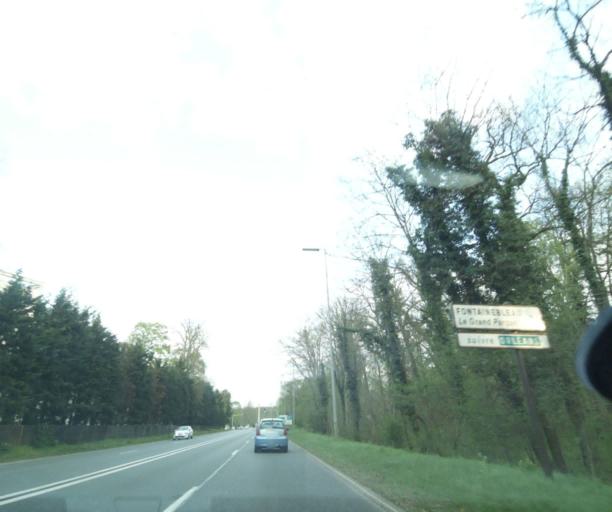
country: FR
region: Ile-de-France
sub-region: Departement de Seine-et-Marne
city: Fontainebleau
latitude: 48.3992
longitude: 2.6889
